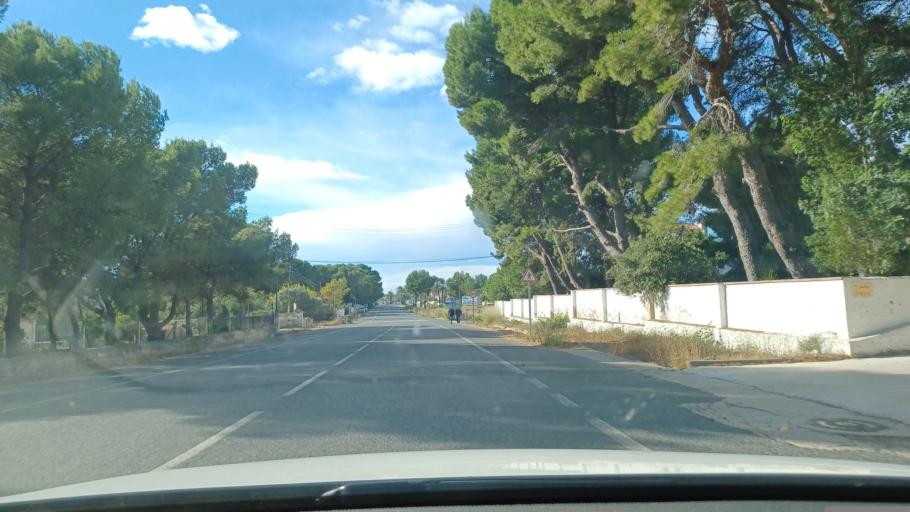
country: ES
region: Catalonia
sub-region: Provincia de Tarragona
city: Sant Carles de la Rapita
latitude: 40.5987
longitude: 0.5737
